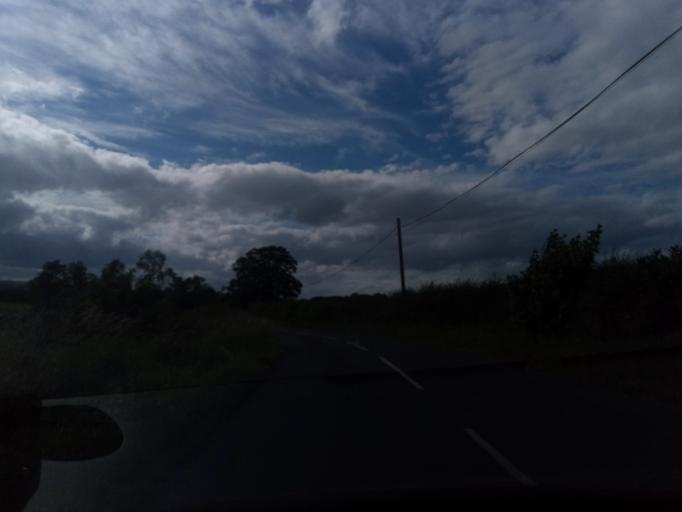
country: GB
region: Scotland
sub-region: The Scottish Borders
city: Coldstream
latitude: 55.5947
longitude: -2.2207
